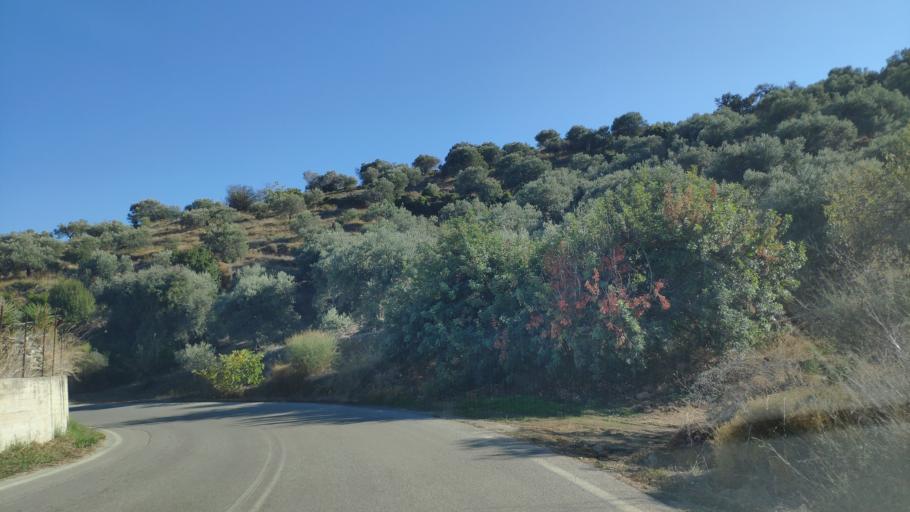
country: GR
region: Attica
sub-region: Nomos Piraios
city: Galatas
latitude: 37.5426
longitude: 23.3662
